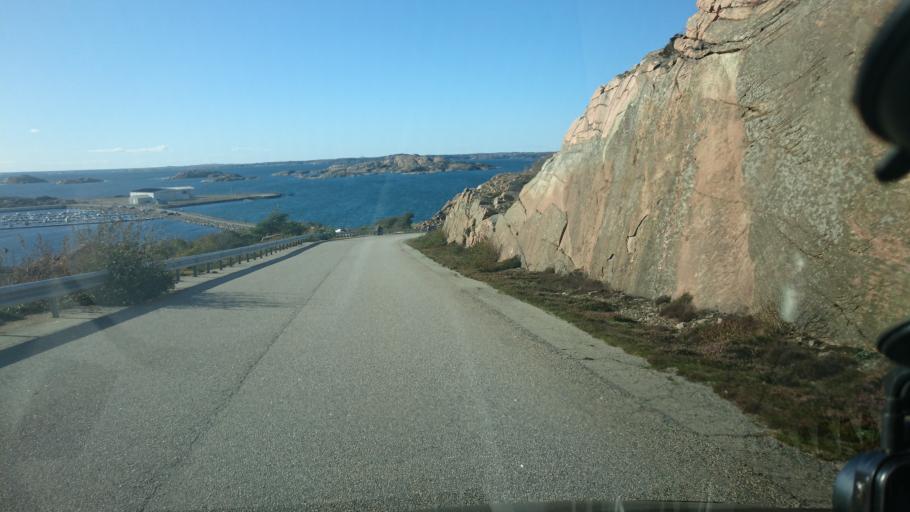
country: SE
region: Vaestra Goetaland
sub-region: Lysekils Kommun
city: Lysekil
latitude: 58.3167
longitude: 11.4058
